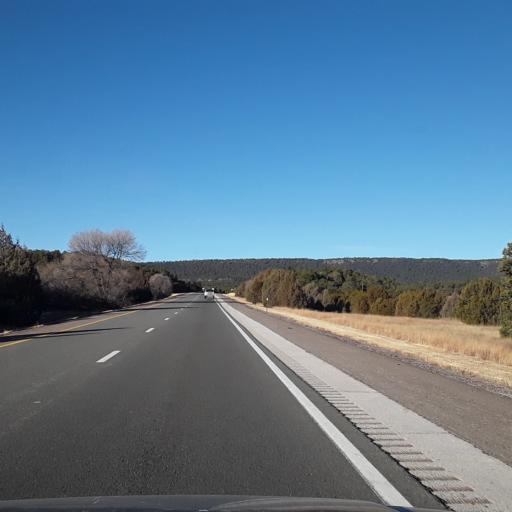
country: US
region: New Mexico
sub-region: San Miguel County
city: Pecos
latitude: 35.5549
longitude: -105.7260
